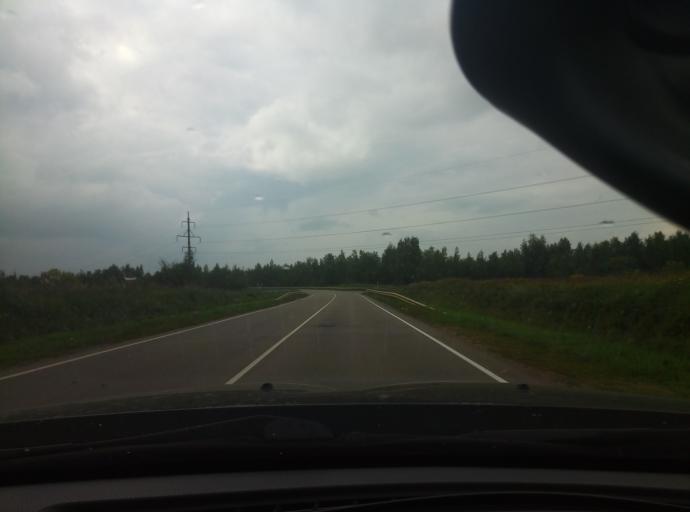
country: RU
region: Tula
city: Lomintsevskiy
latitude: 53.9423
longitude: 37.6290
